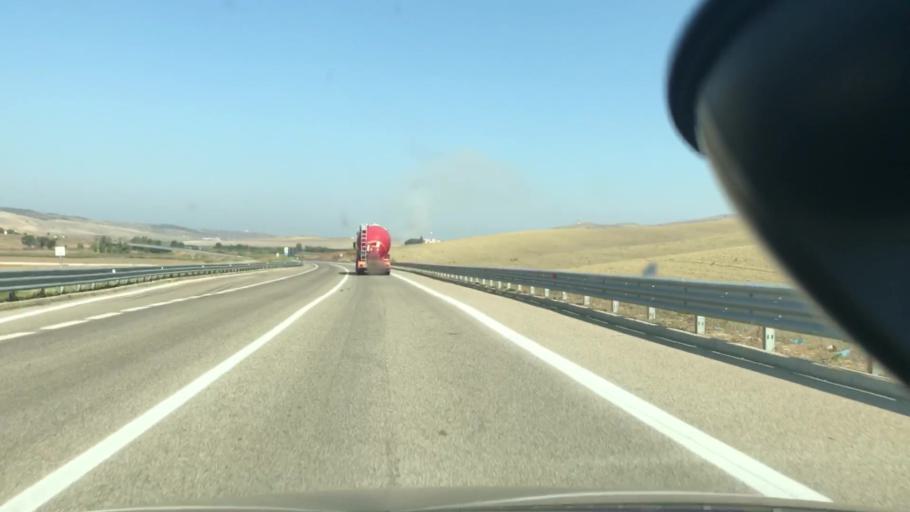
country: IT
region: Basilicate
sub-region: Provincia di Matera
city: Irsina
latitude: 40.7781
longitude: 16.3179
